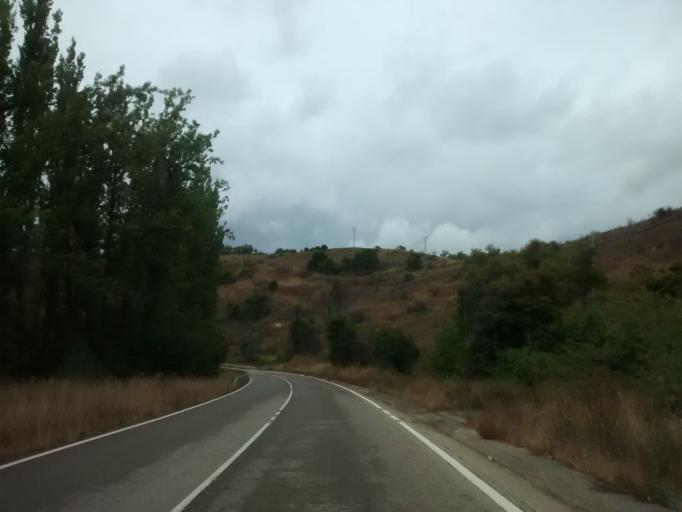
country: ES
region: Castille and Leon
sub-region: Provincia de Palencia
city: Berzosilla
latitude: 42.8565
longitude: -4.0392
